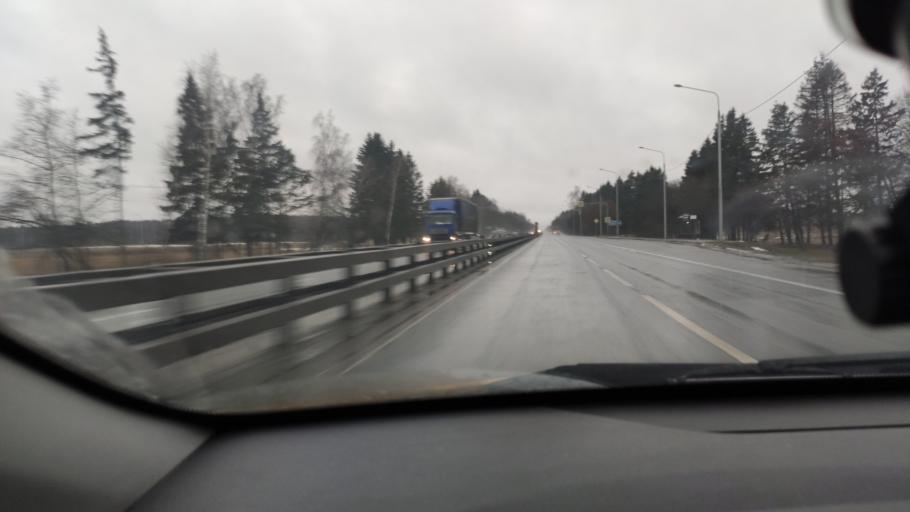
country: RU
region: Moskovskaya
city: Troitsk
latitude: 55.3363
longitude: 37.2976
